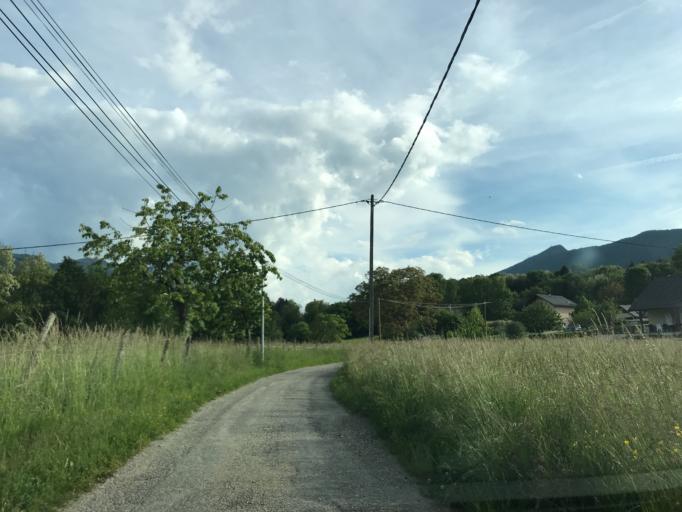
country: FR
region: Rhone-Alpes
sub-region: Departement de la Savoie
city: Vimines
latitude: 45.5578
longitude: 5.8638
